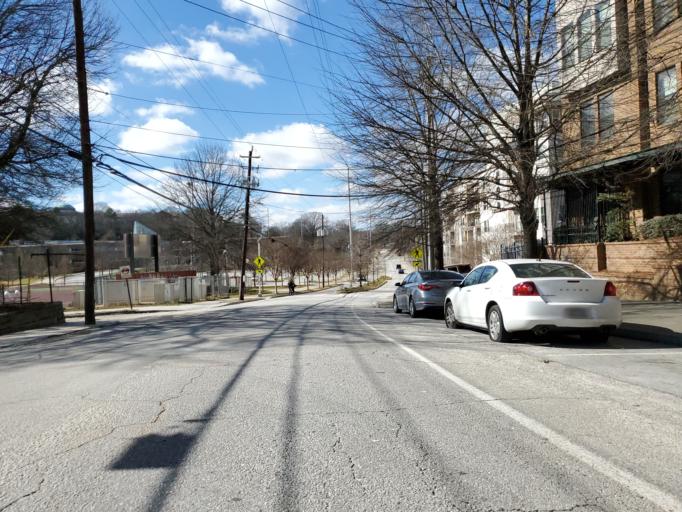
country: US
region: Georgia
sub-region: Fulton County
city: Atlanta
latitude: 33.7398
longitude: -84.3590
